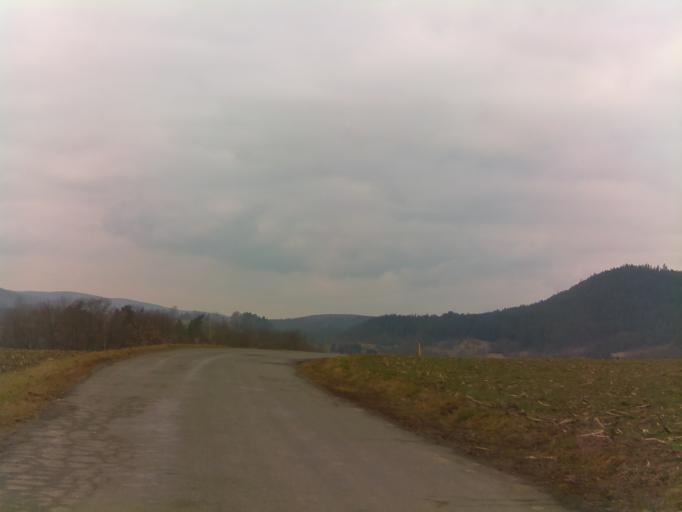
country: DE
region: Thuringia
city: Bad Blankenburg
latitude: 50.7008
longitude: 11.2377
